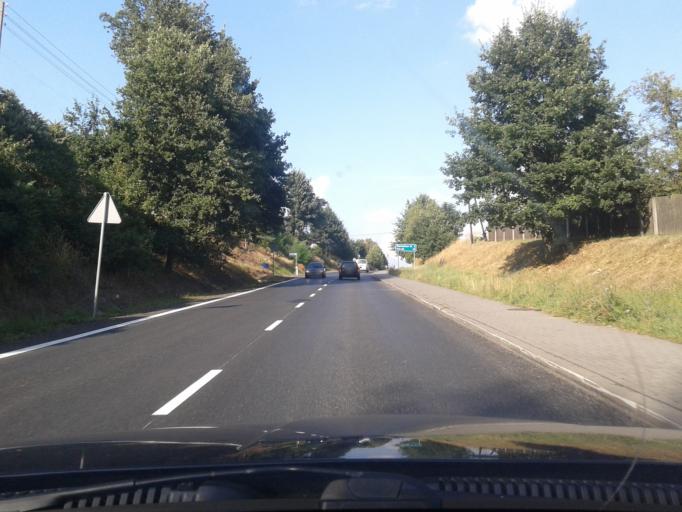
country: PL
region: Silesian Voivodeship
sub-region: Powiat wodzislawski
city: Turza Slaska
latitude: 49.9773
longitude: 18.4483
